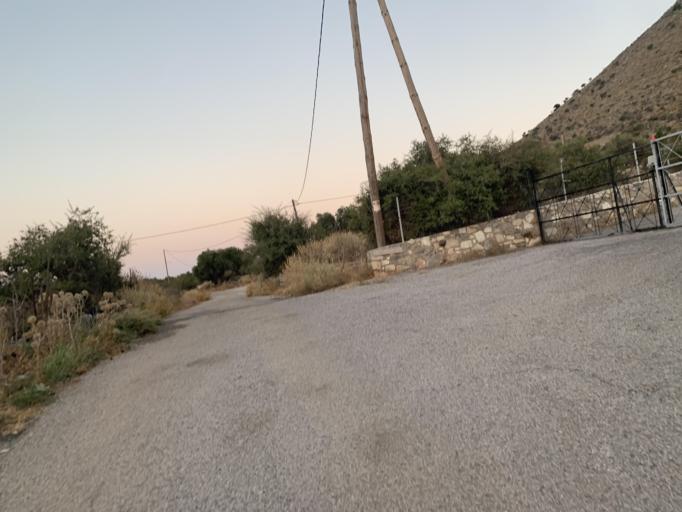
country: GR
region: Crete
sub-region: Nomos Chanias
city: Kalivai
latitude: 35.4516
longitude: 24.2361
